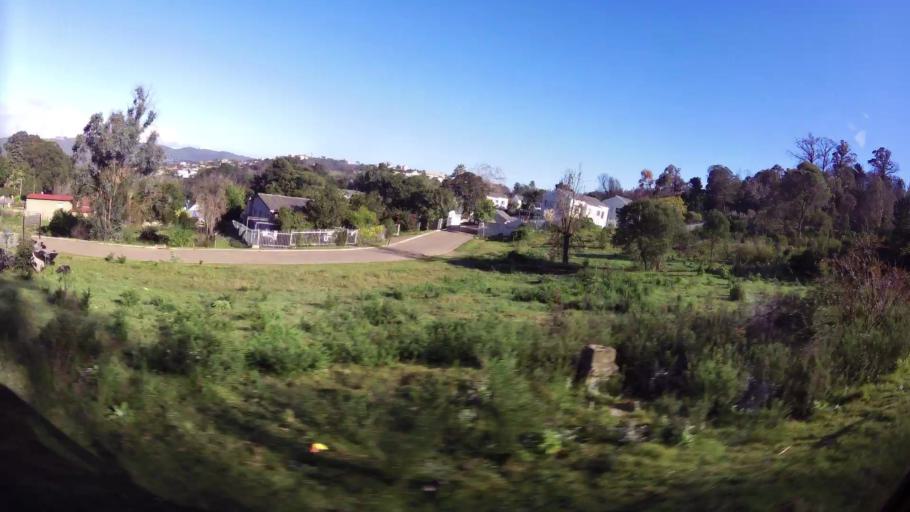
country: ZA
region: Western Cape
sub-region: Eden District Municipality
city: Knysna
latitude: -34.0289
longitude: 23.0516
